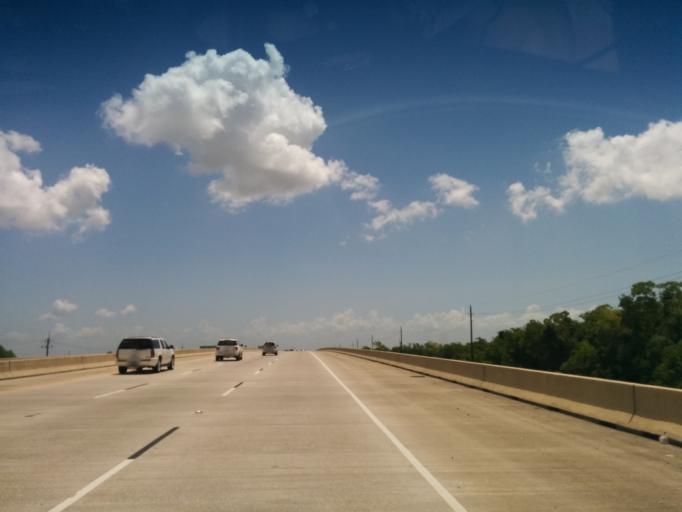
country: US
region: Texas
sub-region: Chambers County
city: Mont Belvieu
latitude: 29.8241
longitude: -94.8686
